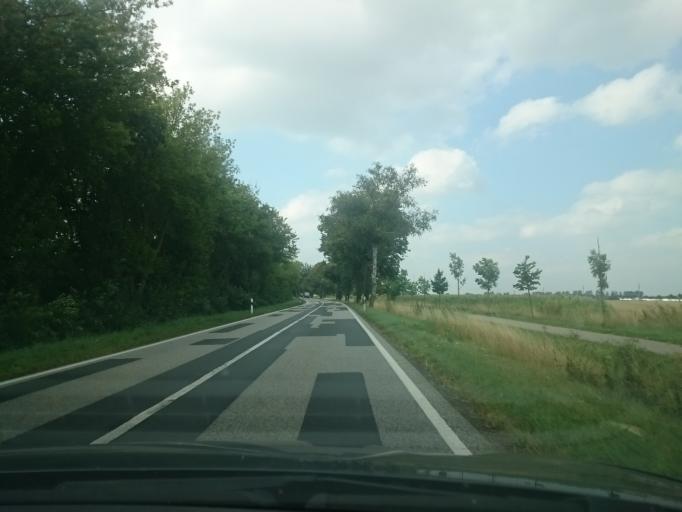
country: DE
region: Mecklenburg-Vorpommern
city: Ducherow
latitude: 53.7477
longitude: 13.7819
